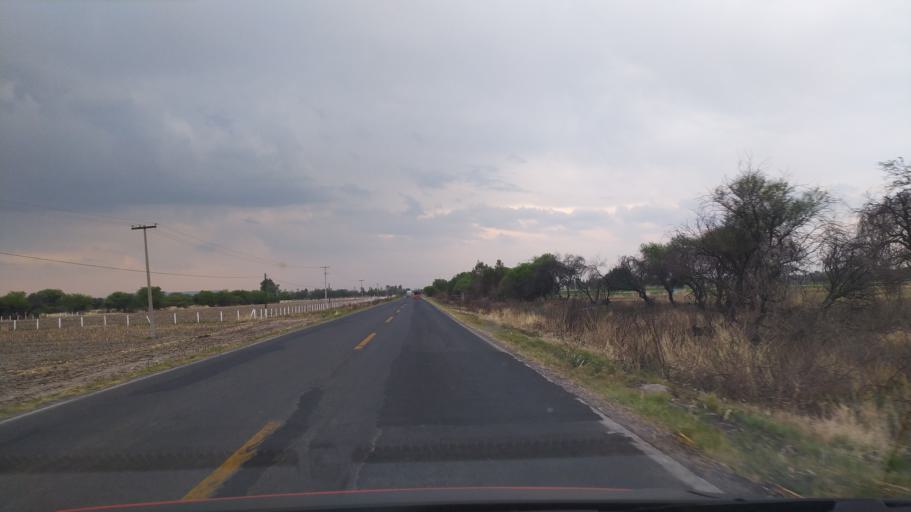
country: MX
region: Guanajuato
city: Ciudad Manuel Doblado
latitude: 20.7764
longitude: -101.9111
